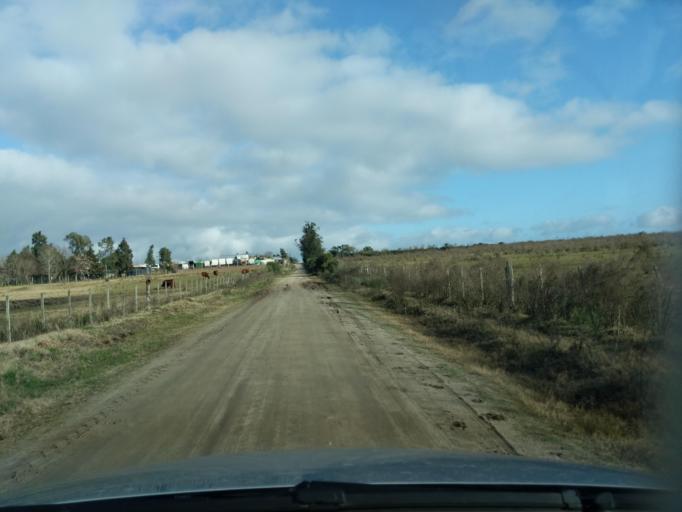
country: UY
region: Florida
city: Florida
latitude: -34.0785
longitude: -56.2170
